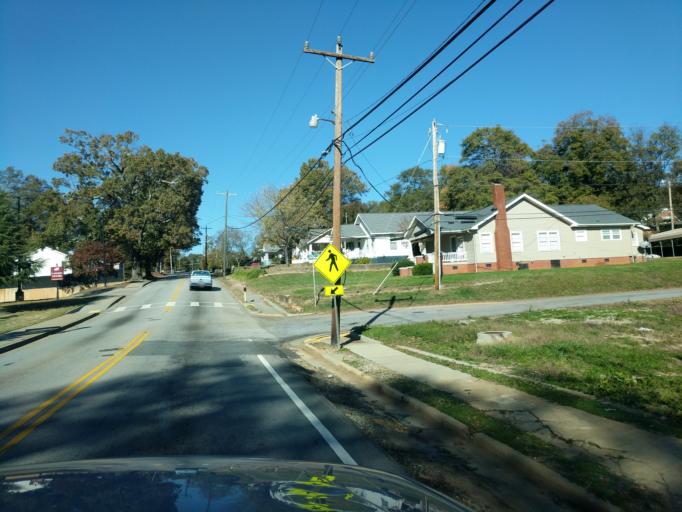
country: US
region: South Carolina
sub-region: Greenville County
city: Greer
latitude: 34.9384
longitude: -82.2223
